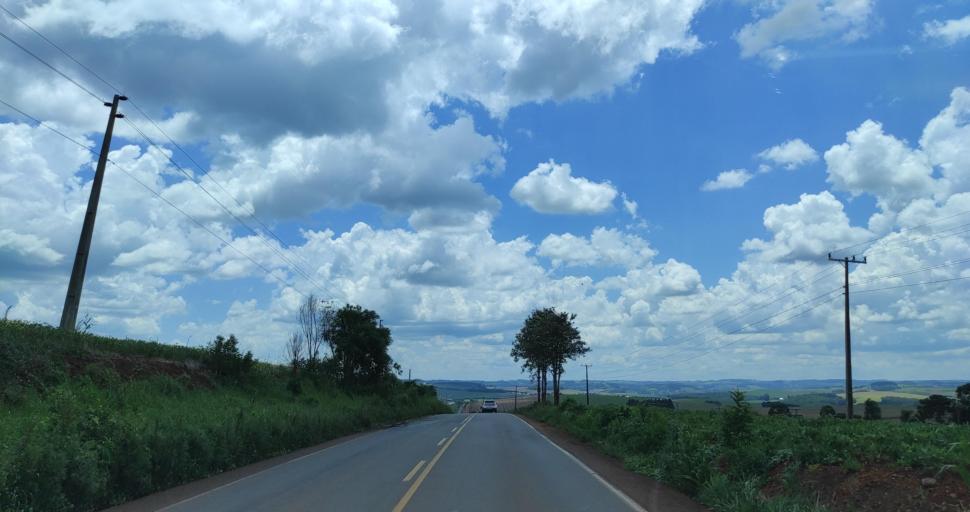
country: BR
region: Santa Catarina
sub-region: Xanxere
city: Xanxere
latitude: -26.7808
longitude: -52.4073
